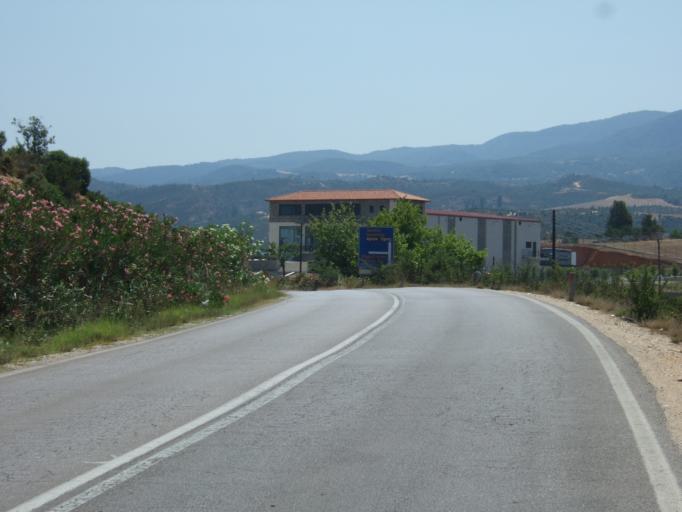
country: GR
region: Central Macedonia
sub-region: Nomos Thessalonikis
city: Nea Apollonia
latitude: 40.5058
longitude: 23.4693
